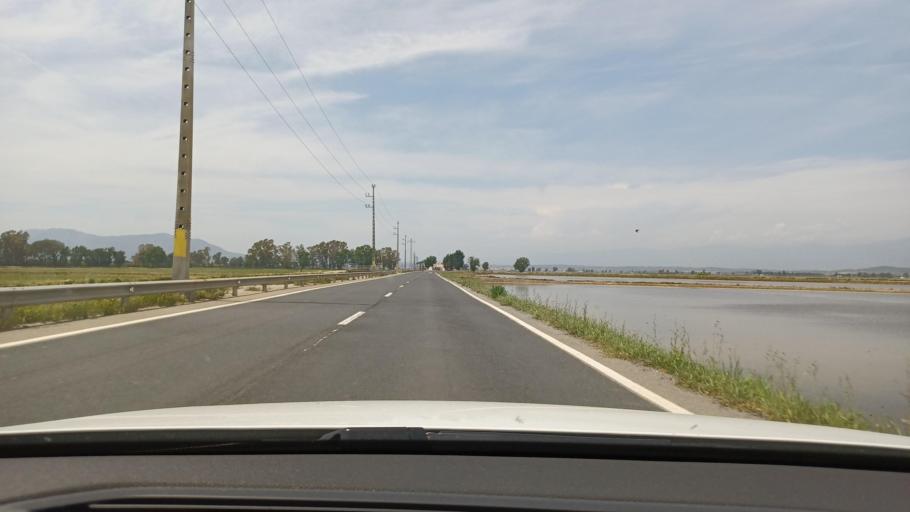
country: ES
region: Catalonia
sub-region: Provincia de Tarragona
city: Deltebre
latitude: 40.7235
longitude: 0.6614
